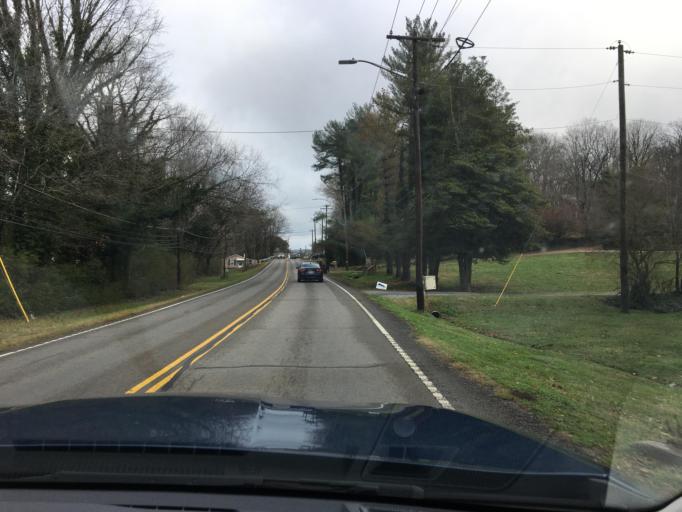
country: US
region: Tennessee
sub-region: McMinn County
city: Athens
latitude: 35.4407
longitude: -84.6133
